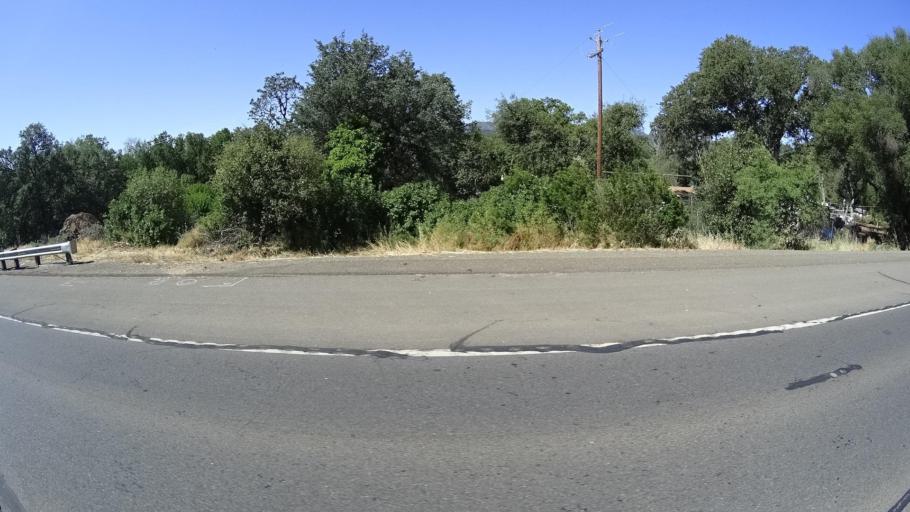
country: US
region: California
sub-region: Lake County
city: Lower Lake
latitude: 38.9265
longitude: -122.6162
